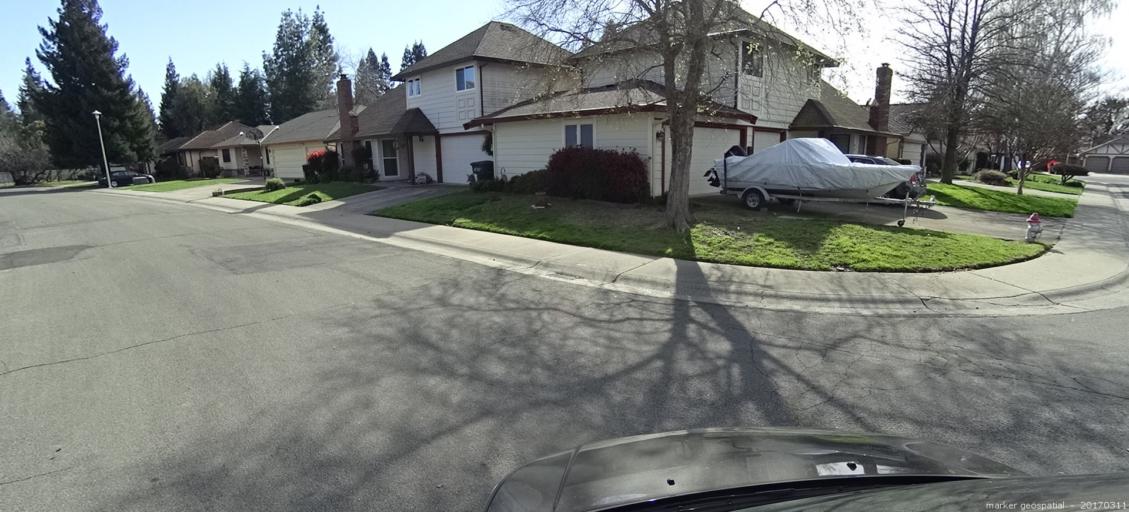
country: US
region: California
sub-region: Yolo County
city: West Sacramento
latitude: 38.4986
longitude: -121.5434
